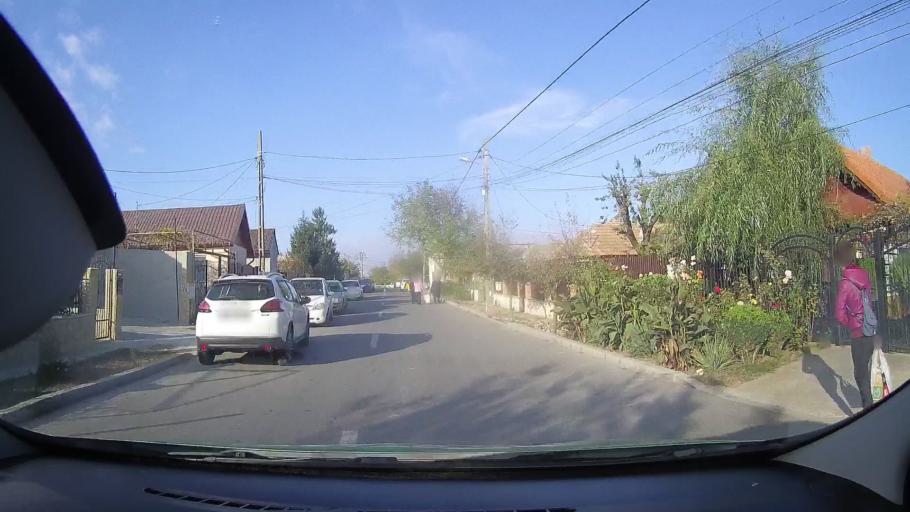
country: RO
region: Constanta
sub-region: Comuna Lumina
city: Lumina
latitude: 44.2865
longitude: 28.5649
